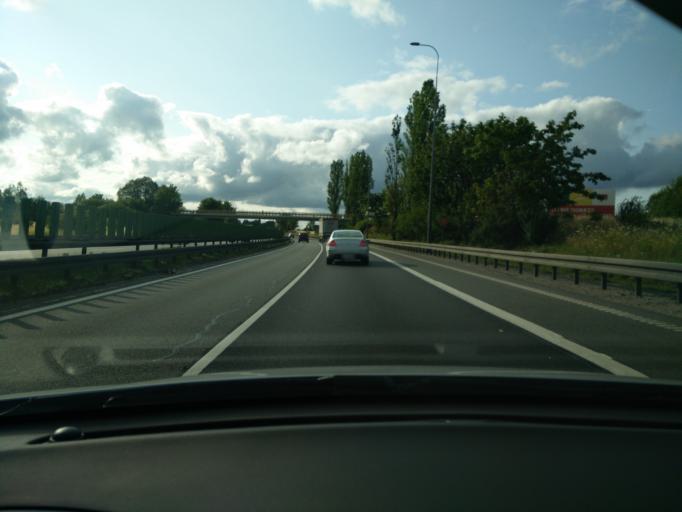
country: PL
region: Pomeranian Voivodeship
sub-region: Powiat gdanski
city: Straszyn
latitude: 54.2964
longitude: 18.5826
